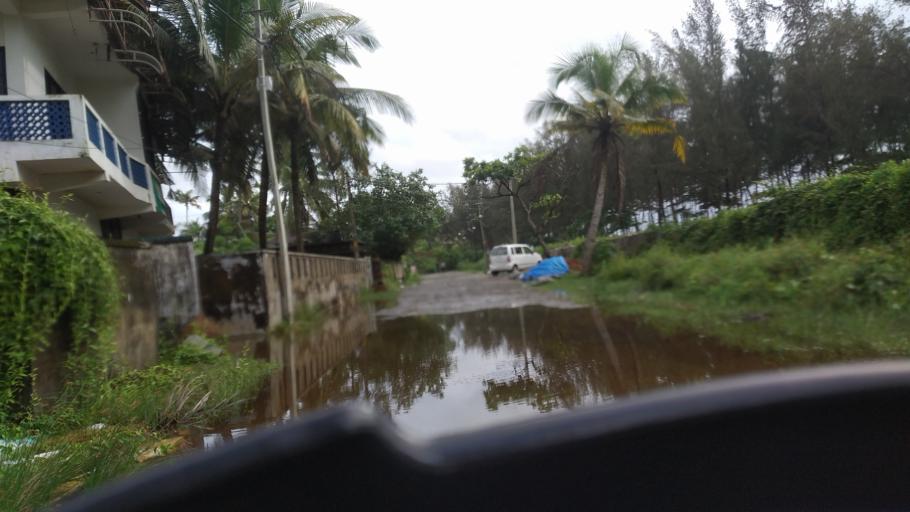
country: IN
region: Kerala
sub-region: Ernakulam
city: Elur
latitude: 10.1049
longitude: 76.1887
